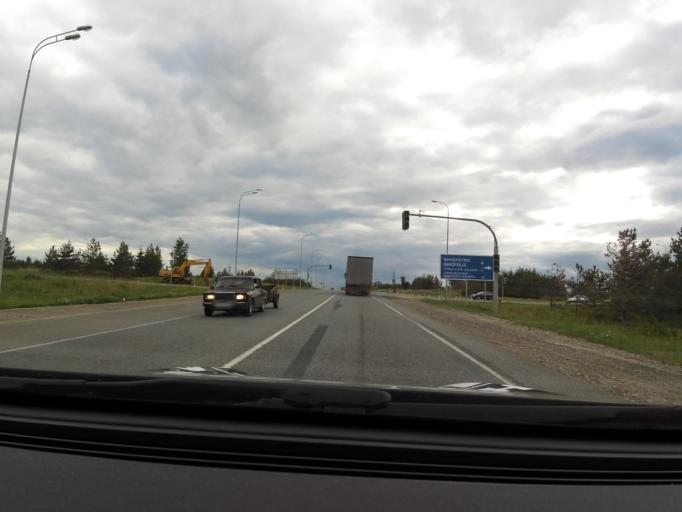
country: RU
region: Tatarstan
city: Sviyazhsk
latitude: 55.7277
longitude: 48.7609
